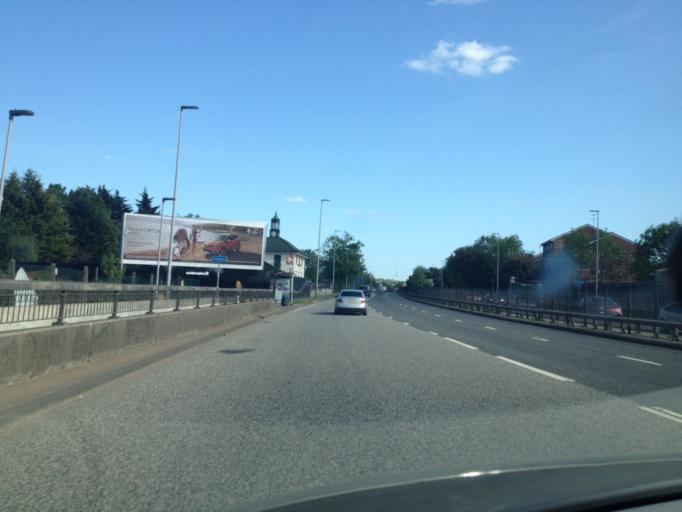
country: GB
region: England
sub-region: Greater London
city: Hendon
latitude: 51.5750
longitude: -0.2141
